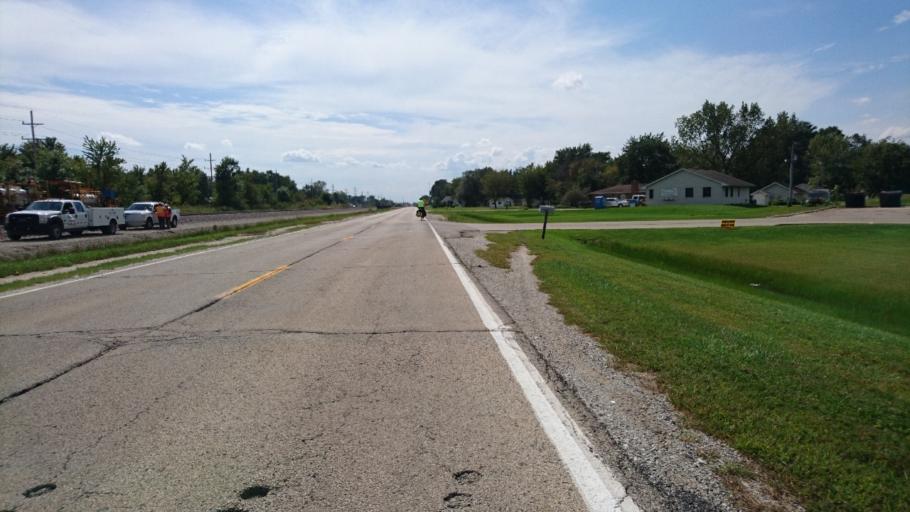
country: US
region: Illinois
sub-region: Grundy County
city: Central City
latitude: 41.2277
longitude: -88.2584
